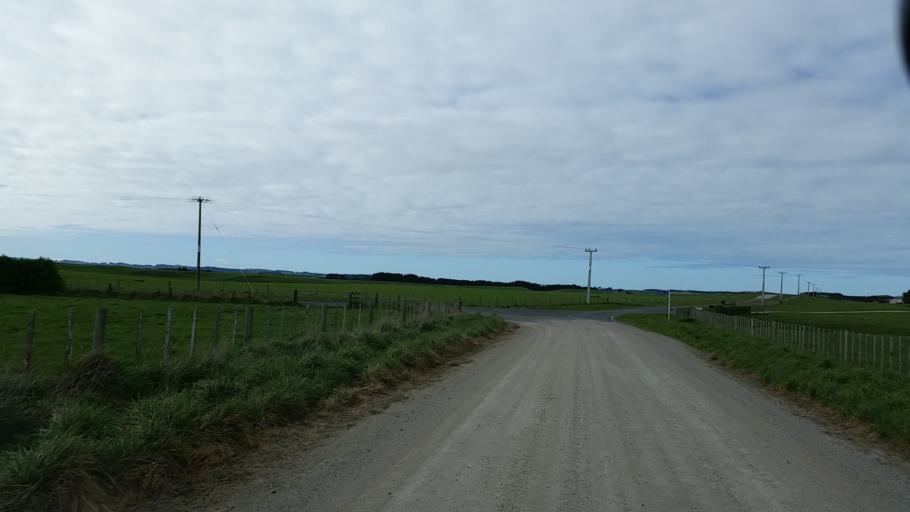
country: NZ
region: Taranaki
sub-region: South Taranaki District
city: Patea
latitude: -39.8026
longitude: 174.6897
